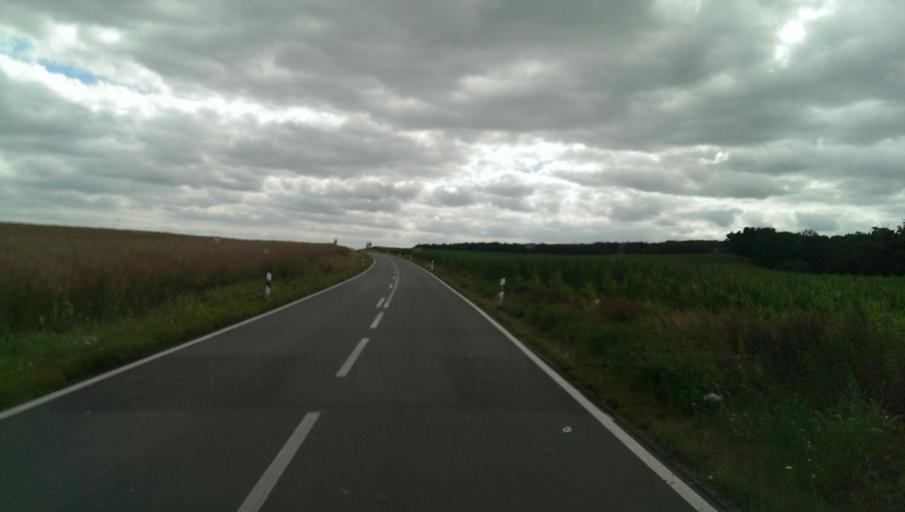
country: DE
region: Brandenburg
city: Belzig
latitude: 52.1095
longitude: 12.6222
